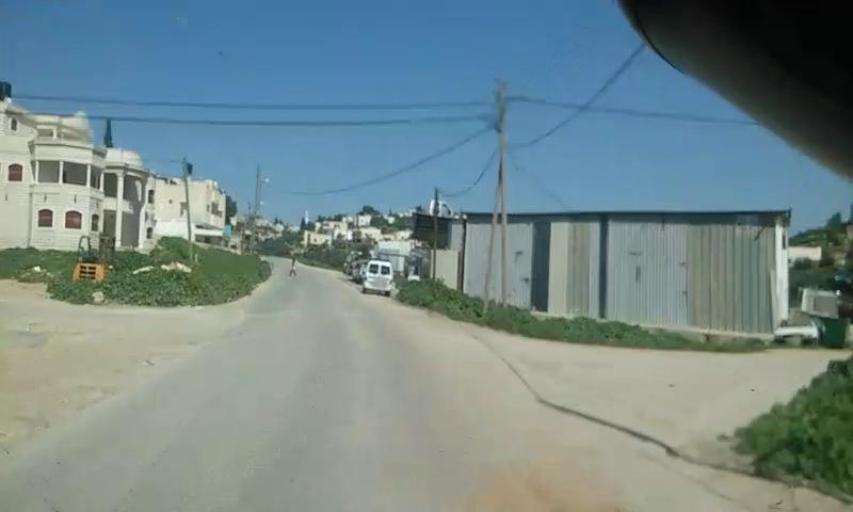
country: PS
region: West Bank
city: Idhna
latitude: 31.5504
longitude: 34.9681
